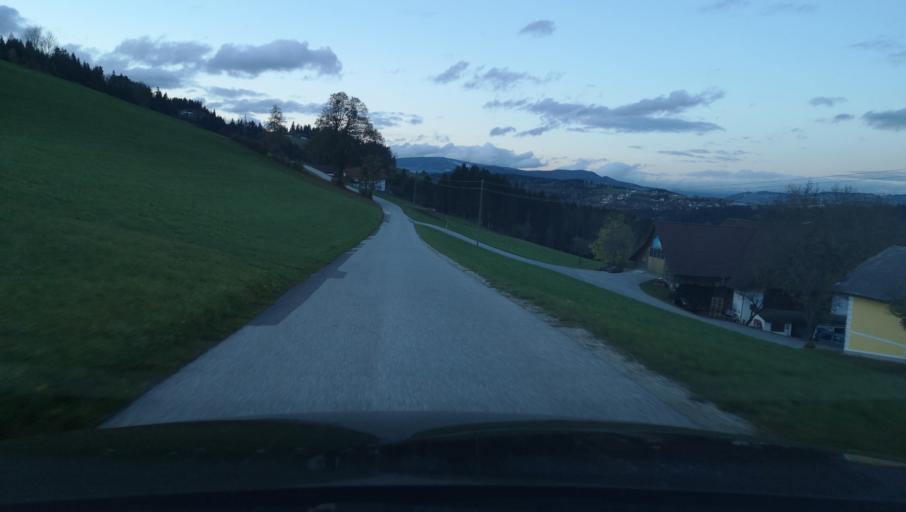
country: AT
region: Styria
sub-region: Politischer Bezirk Weiz
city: Koglhof
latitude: 47.3268
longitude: 15.6862
